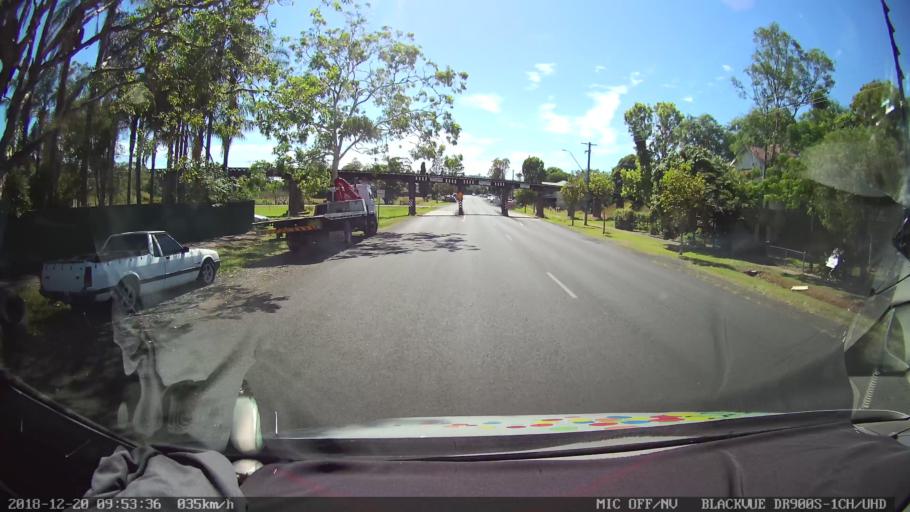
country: AU
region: New South Wales
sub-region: Lismore Municipality
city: Lismore
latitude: -28.8020
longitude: 153.2706
